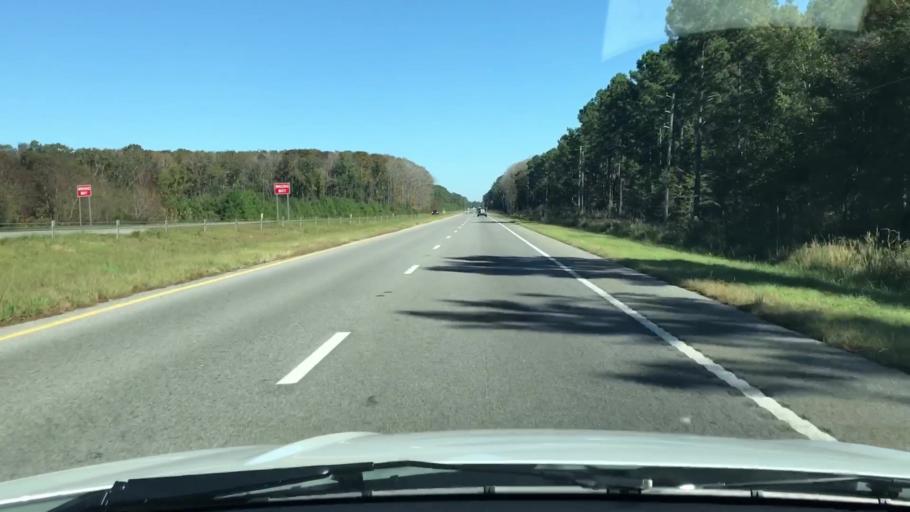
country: US
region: South Carolina
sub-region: Colleton County
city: Walterboro
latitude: 32.7680
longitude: -80.4915
